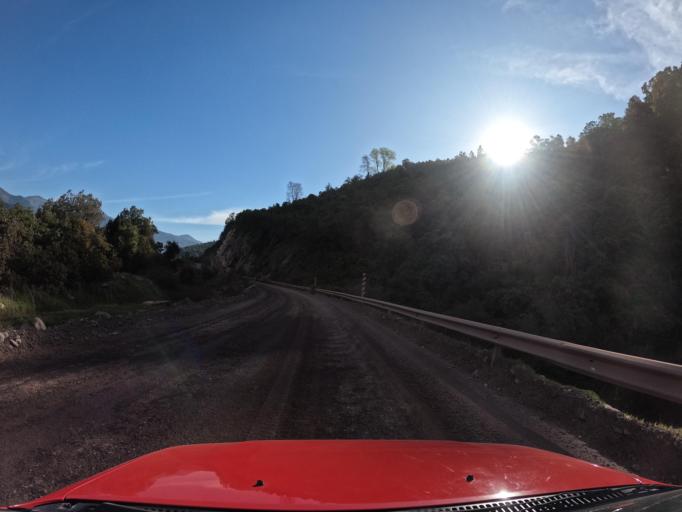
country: CL
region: O'Higgins
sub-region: Provincia de Colchagua
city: Chimbarongo
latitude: -34.9955
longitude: -70.8200
